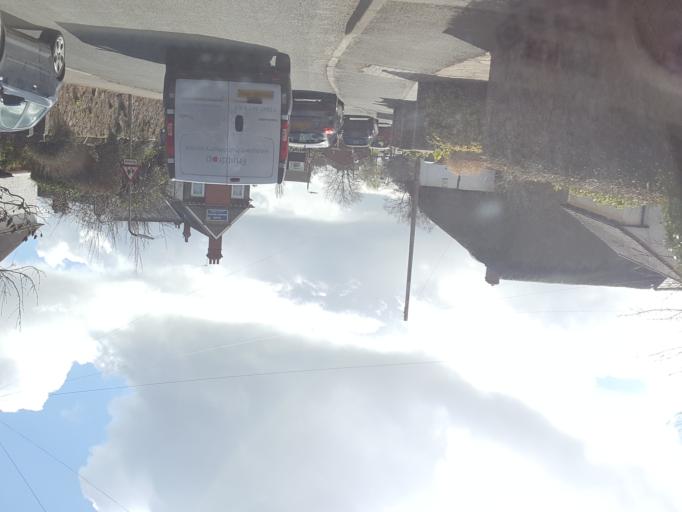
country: GB
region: England
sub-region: Worcestershire
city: Great Malvern
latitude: 52.1046
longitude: -2.3188
